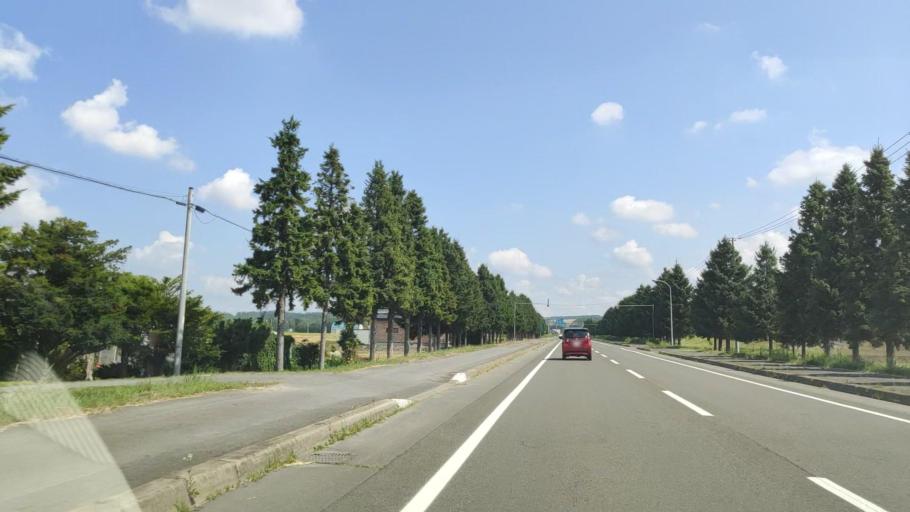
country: JP
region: Hokkaido
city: Shimo-furano
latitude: 43.4808
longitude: 142.4607
